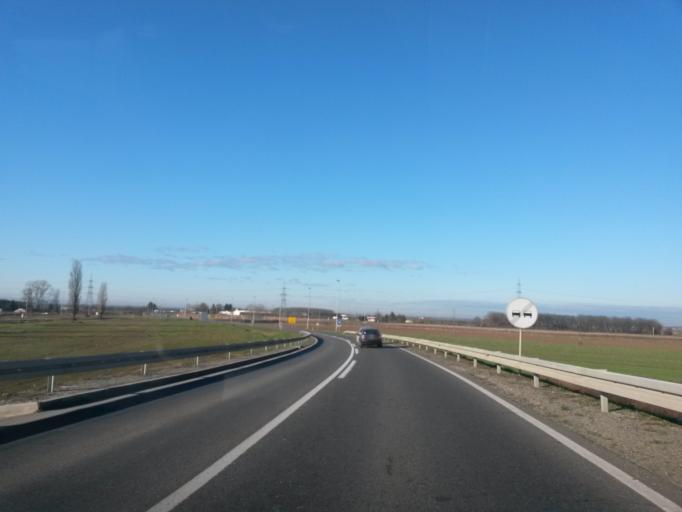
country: HR
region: Osjecko-Baranjska
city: Josipovac
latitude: 45.5851
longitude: 18.5653
